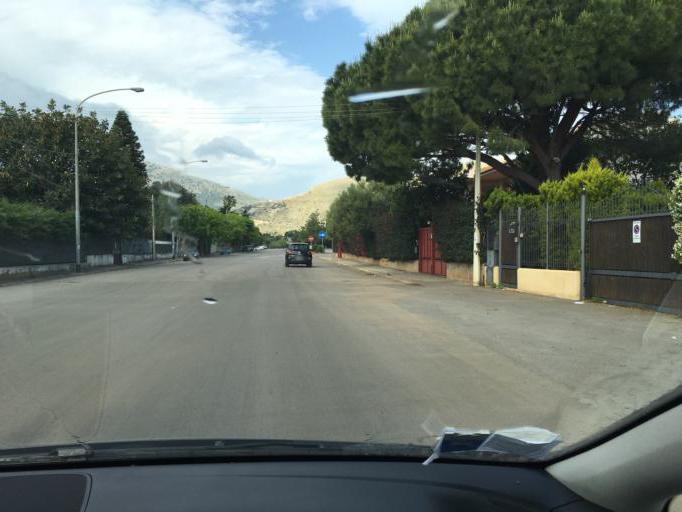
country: IT
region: Sicily
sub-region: Palermo
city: Palermo
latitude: 38.2031
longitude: 13.3198
